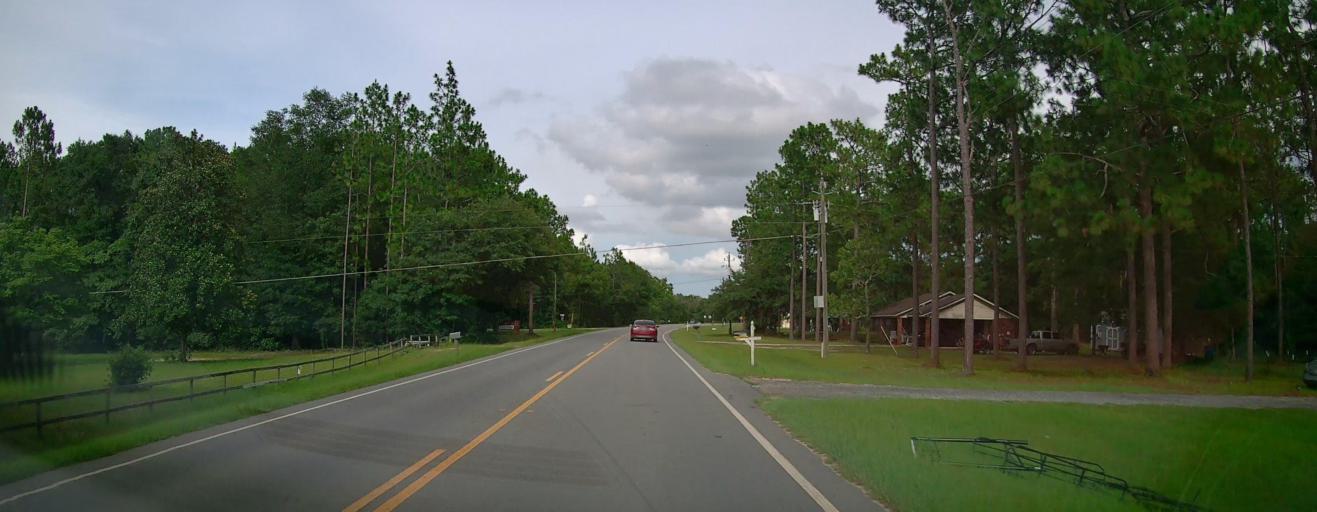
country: US
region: Georgia
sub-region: Wayne County
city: Jesup
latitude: 31.6573
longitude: -81.8992
